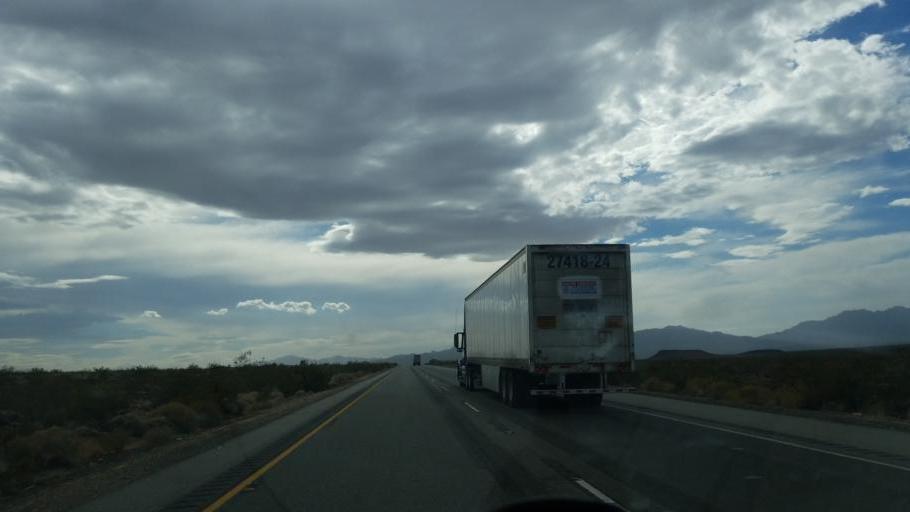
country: US
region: California
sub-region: San Bernardino County
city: Needles
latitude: 34.8030
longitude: -115.3371
